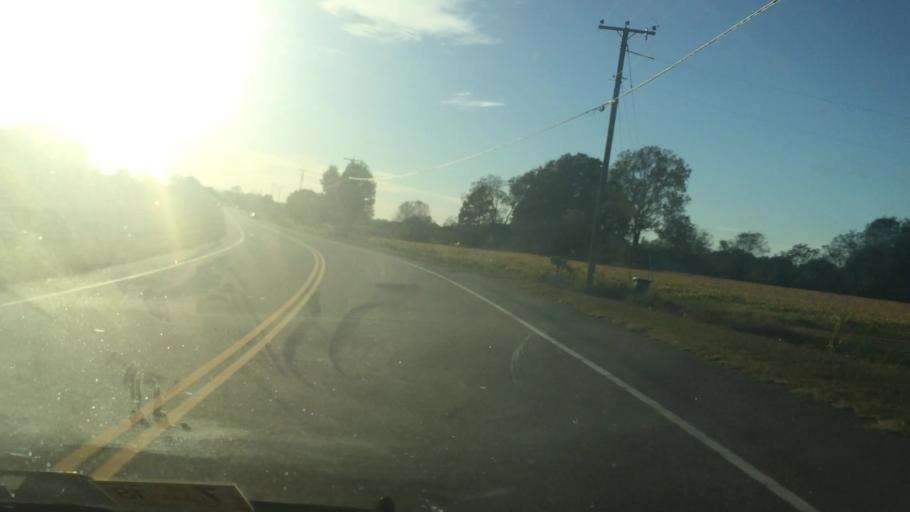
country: US
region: Virginia
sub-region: James City County
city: Williamsburg
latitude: 37.3850
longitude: -76.8166
